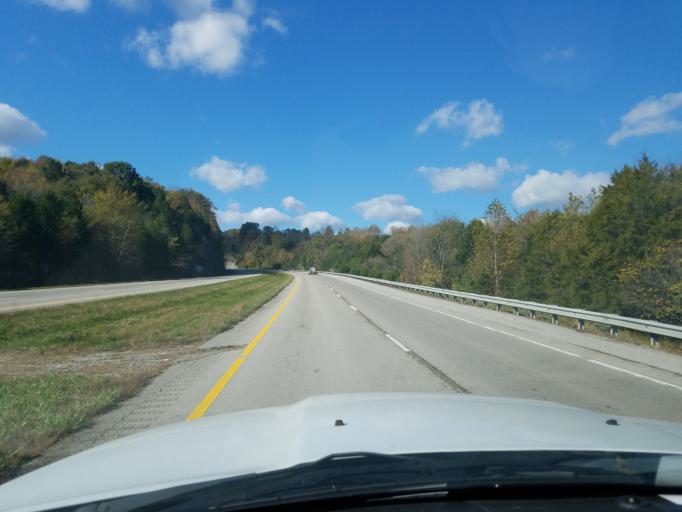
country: US
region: Kentucky
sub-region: Metcalfe County
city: Edmonton
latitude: 37.0269
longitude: -85.5461
